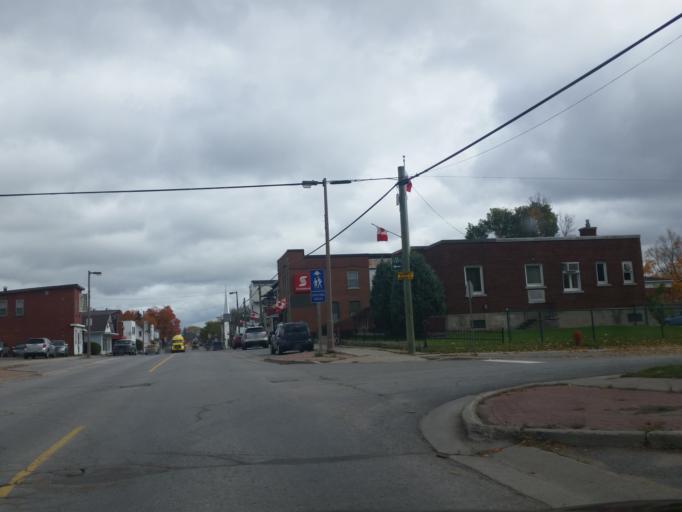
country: CA
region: Ontario
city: Renfrew
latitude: 45.6265
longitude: -76.8854
